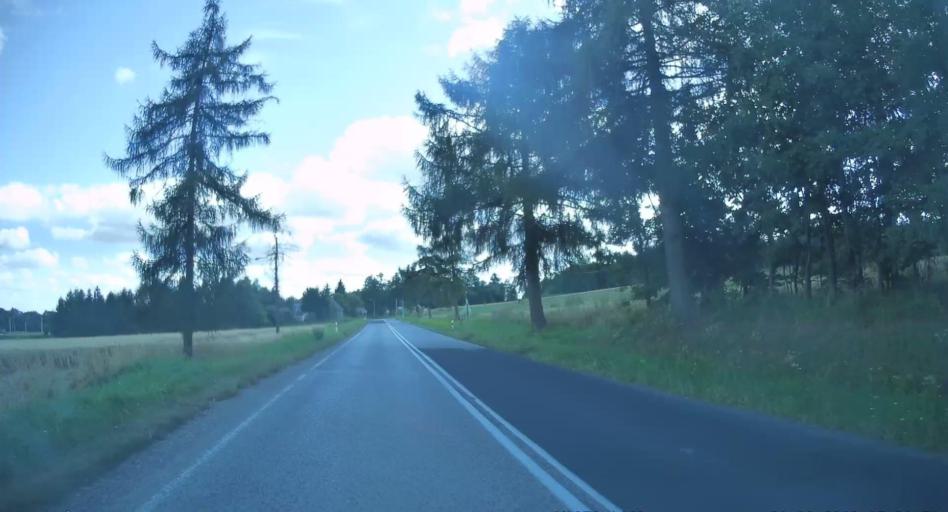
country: PL
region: Swietokrzyskie
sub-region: Powiat kielecki
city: Lagow
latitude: 50.8107
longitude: 21.0797
